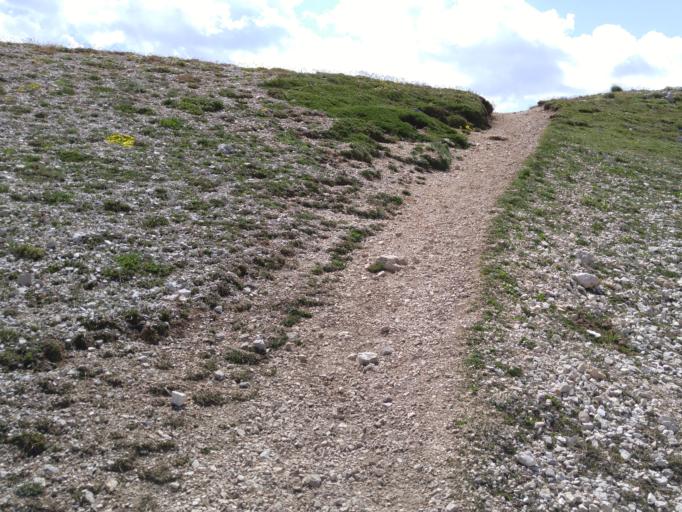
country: IT
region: Abruzzo
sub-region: Provincia di Teramo
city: Pietracamela
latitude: 42.4588
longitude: 13.5638
